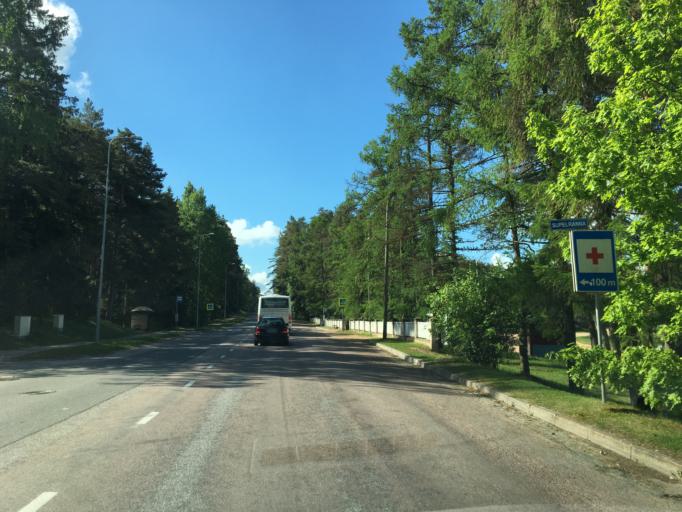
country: EE
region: Tartu
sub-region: Elva linn
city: Elva
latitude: 58.2304
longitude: 26.4075
